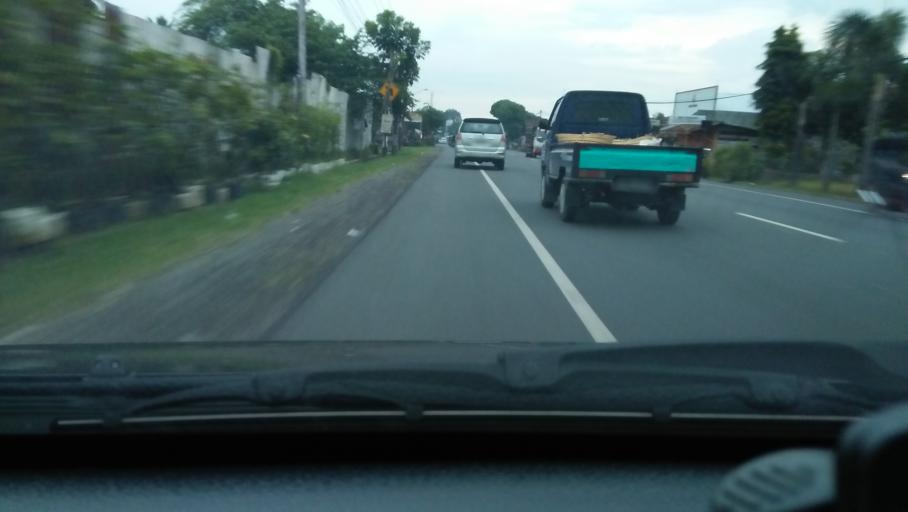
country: ID
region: Central Java
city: Magelang
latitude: -7.4028
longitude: 110.2407
